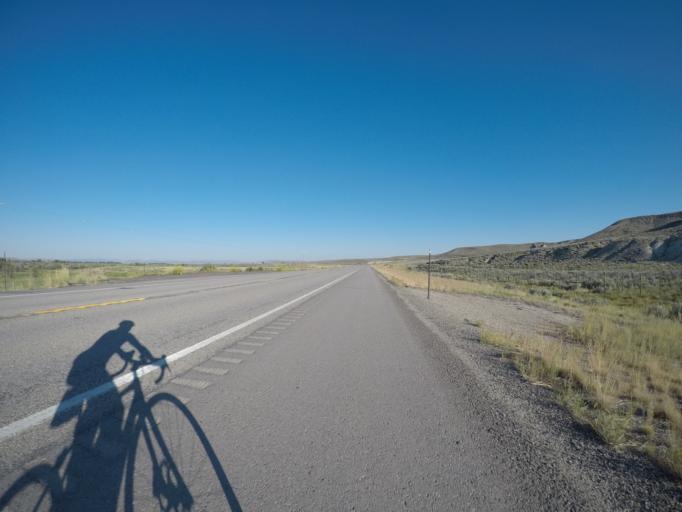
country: US
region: Wyoming
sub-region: Sublette County
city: Pinedale
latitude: 42.8841
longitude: -110.0016
